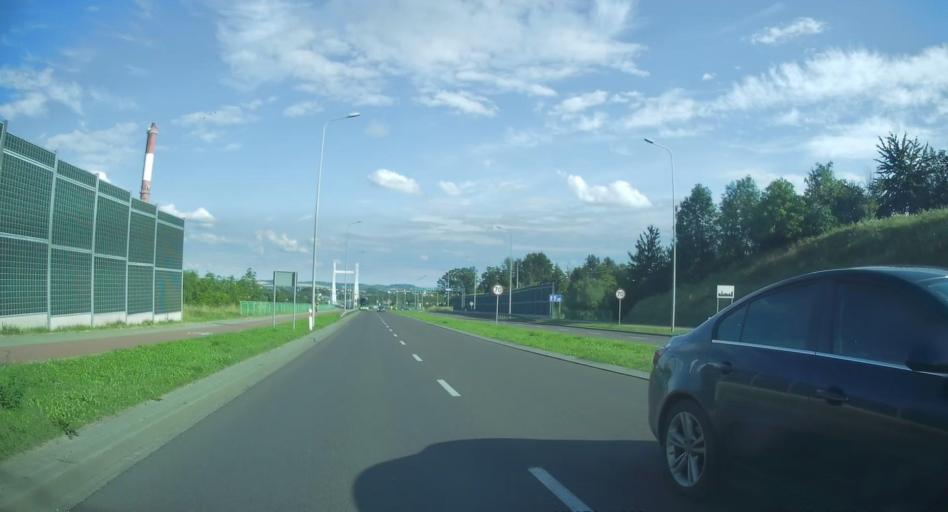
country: PL
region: Subcarpathian Voivodeship
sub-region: Przemysl
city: Przemysl
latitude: 49.8016
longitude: 22.7799
